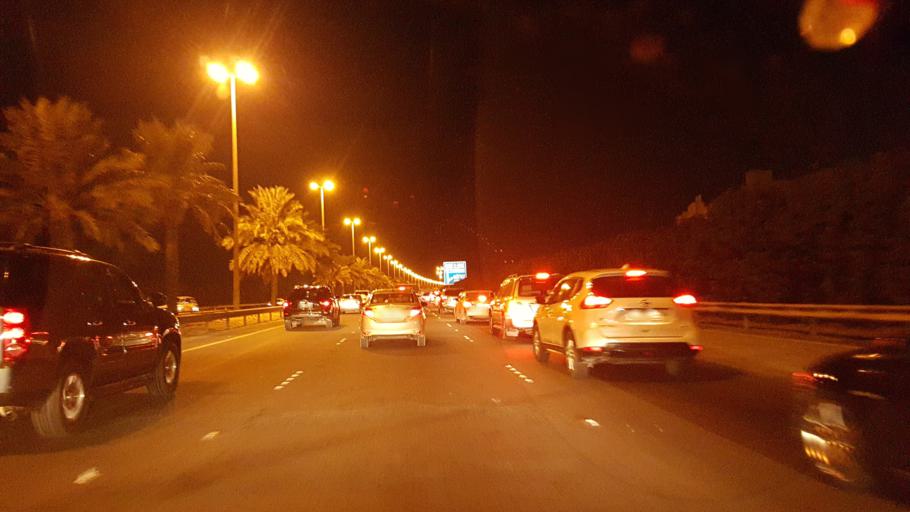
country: BH
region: Central Governorate
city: Madinat Hamad
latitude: 26.1559
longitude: 50.5065
